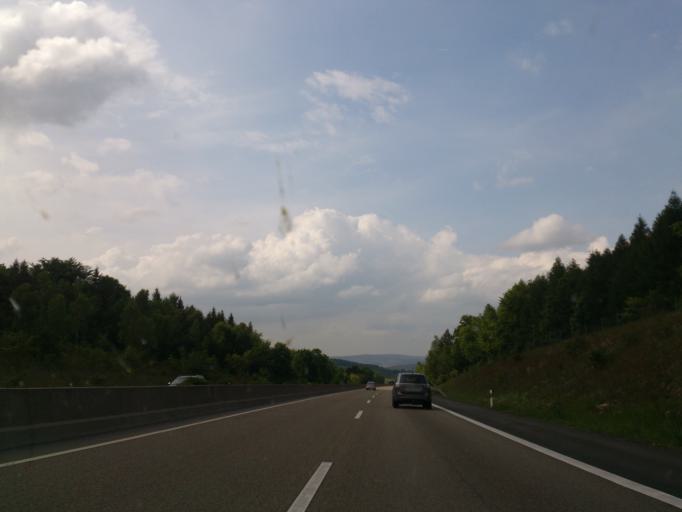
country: DE
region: North Rhine-Westphalia
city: Warburg
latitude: 51.4531
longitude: 9.1291
